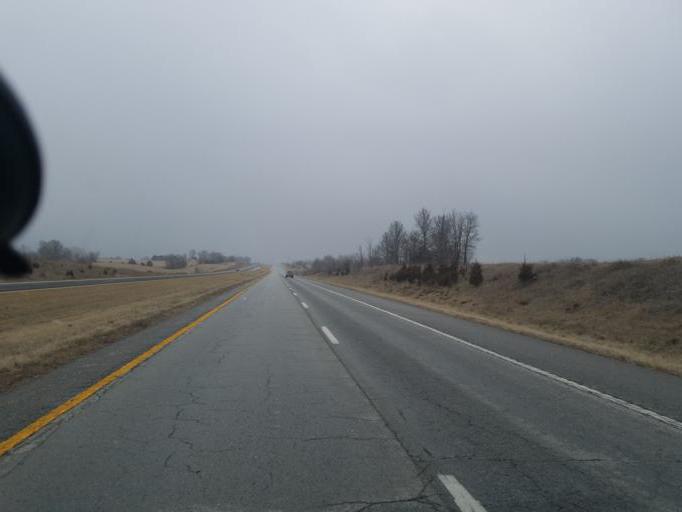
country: US
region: Missouri
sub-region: Macon County
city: La Plata
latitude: 39.9088
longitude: -92.4735
